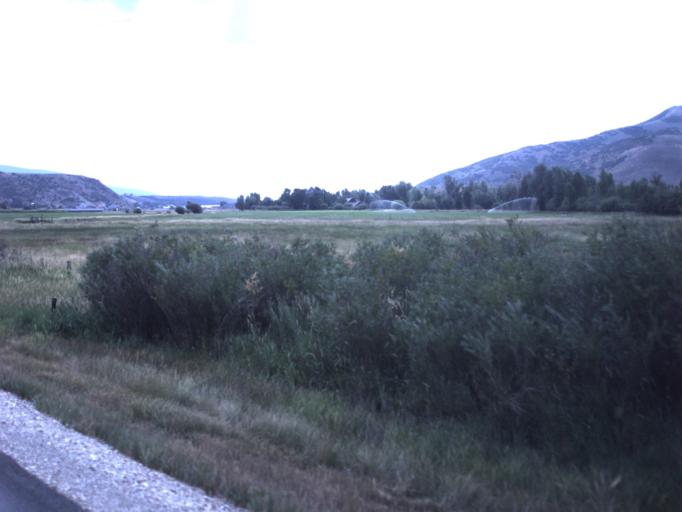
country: US
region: Utah
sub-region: Summit County
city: Oakley
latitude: 40.7499
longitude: -111.3676
